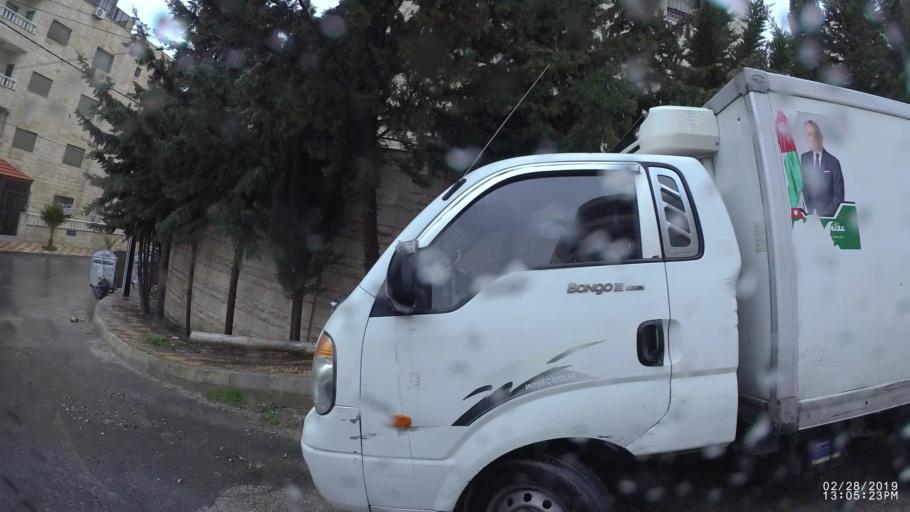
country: JO
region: Amman
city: Al Jubayhah
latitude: 32.0218
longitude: 35.8804
